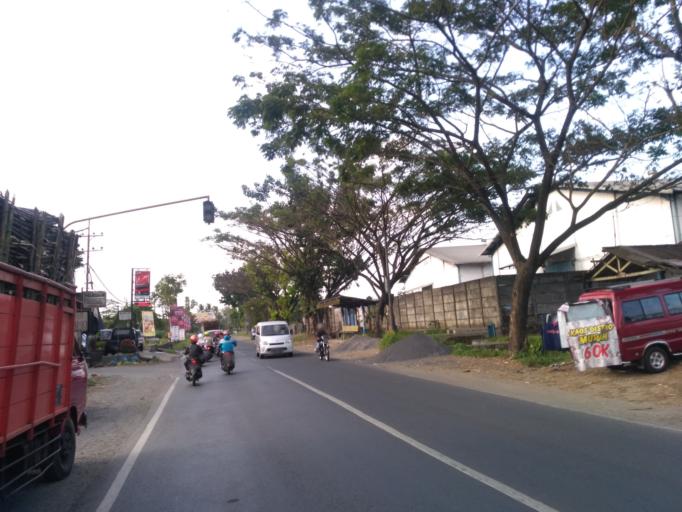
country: ID
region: East Java
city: Wadung
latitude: -8.0432
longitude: 112.6083
